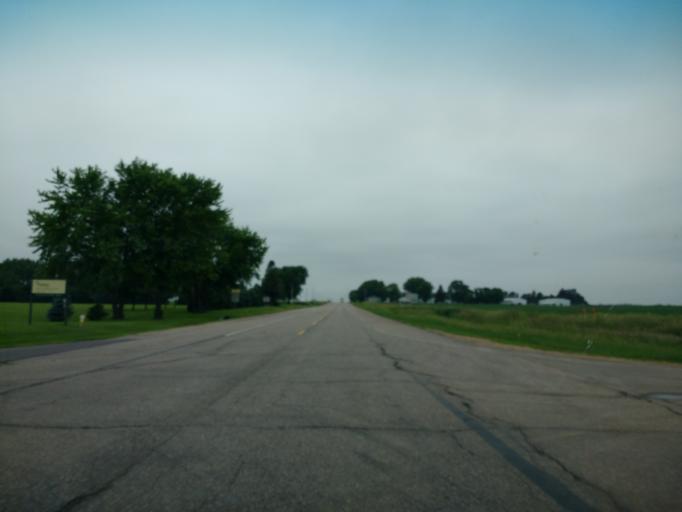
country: US
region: Iowa
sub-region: O'Brien County
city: Hartley
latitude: 43.1850
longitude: -95.4868
